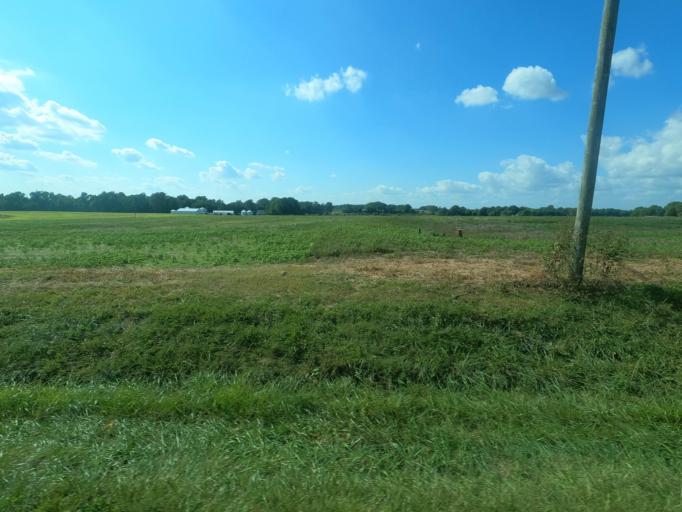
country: US
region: Illinois
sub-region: Massac County
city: Metropolis
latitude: 37.2177
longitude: -88.7292
